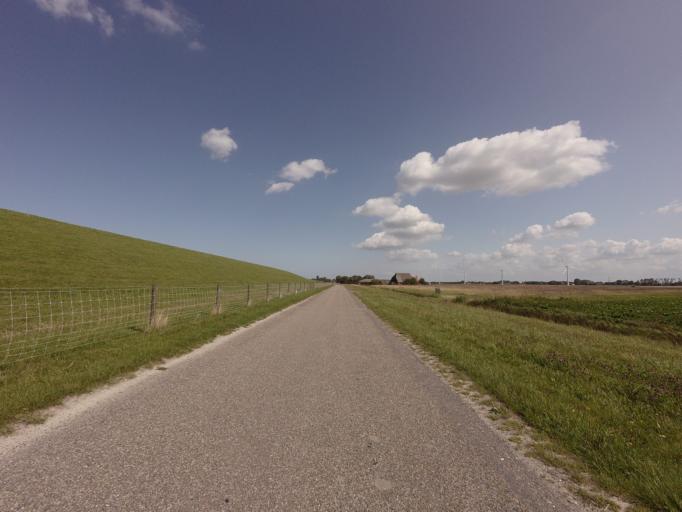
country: NL
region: Friesland
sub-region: Gemeente Ferwerderadiel
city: Hallum
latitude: 53.3224
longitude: 5.7614
